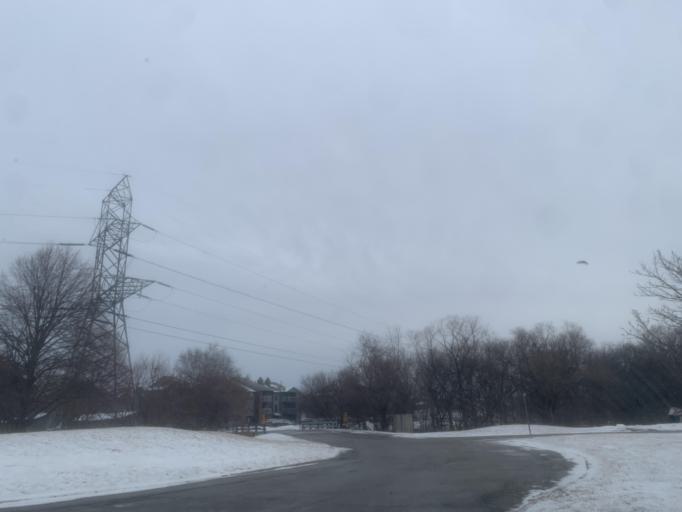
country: US
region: Nebraska
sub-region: Douglas County
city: Ralston
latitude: 41.2722
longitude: -96.0866
